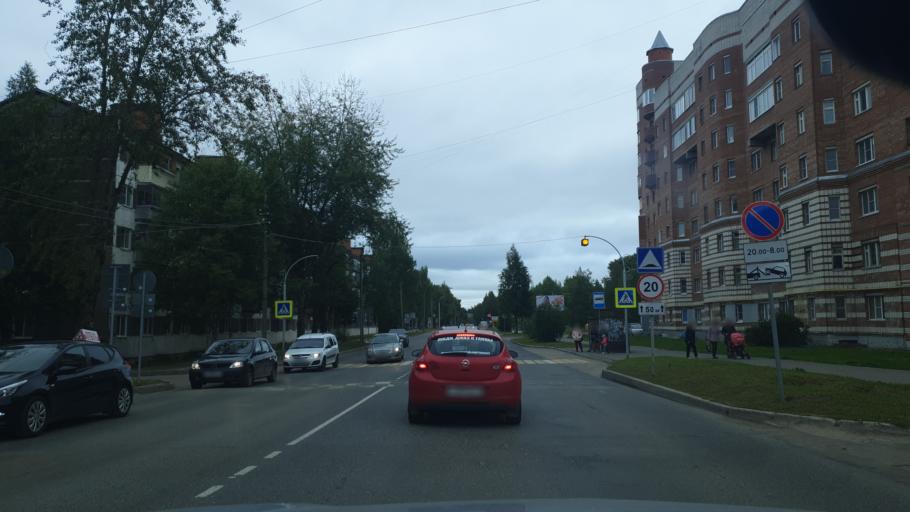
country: RU
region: Komi Republic
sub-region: Syktyvdinskiy Rayon
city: Syktyvkar
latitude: 61.6562
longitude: 50.8038
